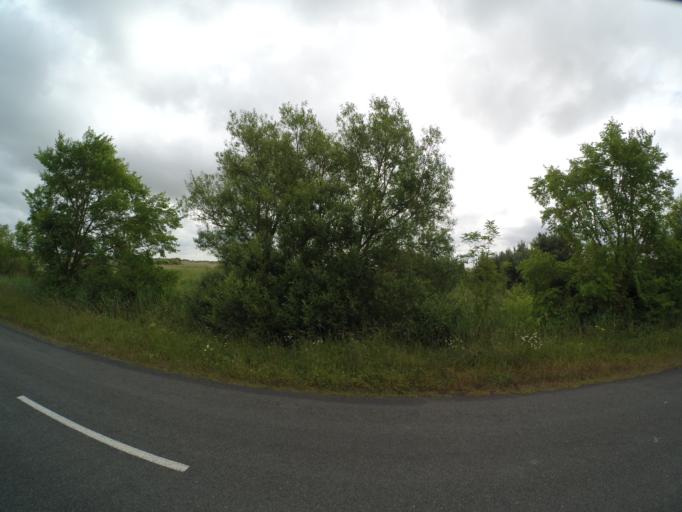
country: FR
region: Poitou-Charentes
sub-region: Departement de la Charente-Maritime
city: Yves
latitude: 46.0330
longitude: -1.0472
